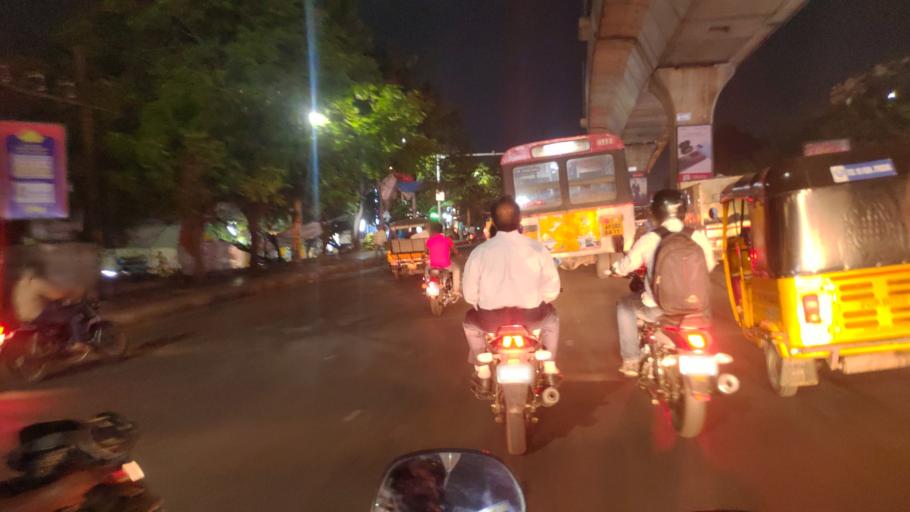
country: IN
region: Telangana
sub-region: Rangareddi
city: Gaddi Annaram
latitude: 17.3699
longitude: 78.5151
